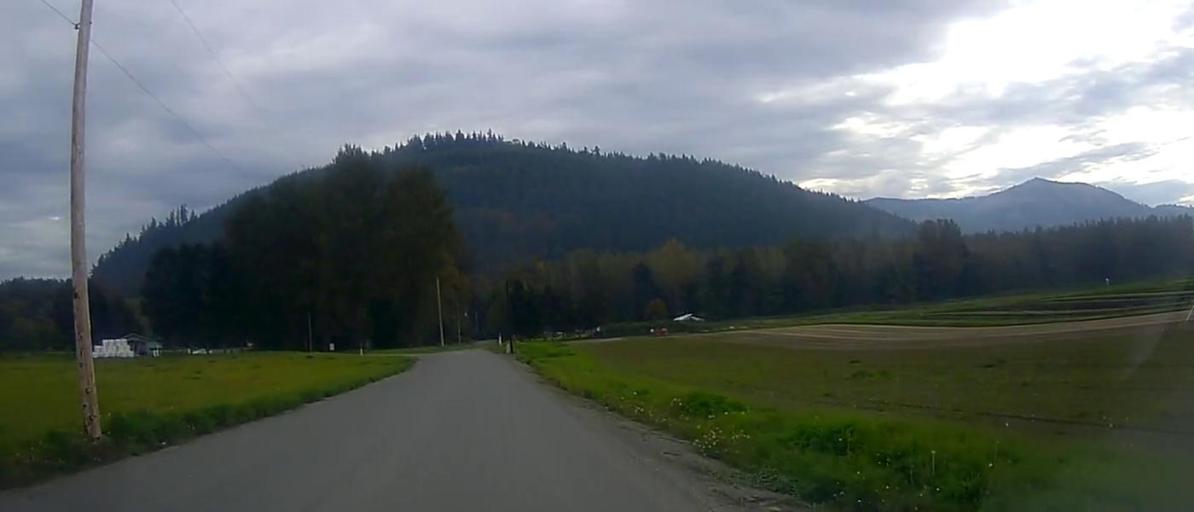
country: US
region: Washington
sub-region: Skagit County
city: Clear Lake
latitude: 48.4786
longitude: -122.2466
